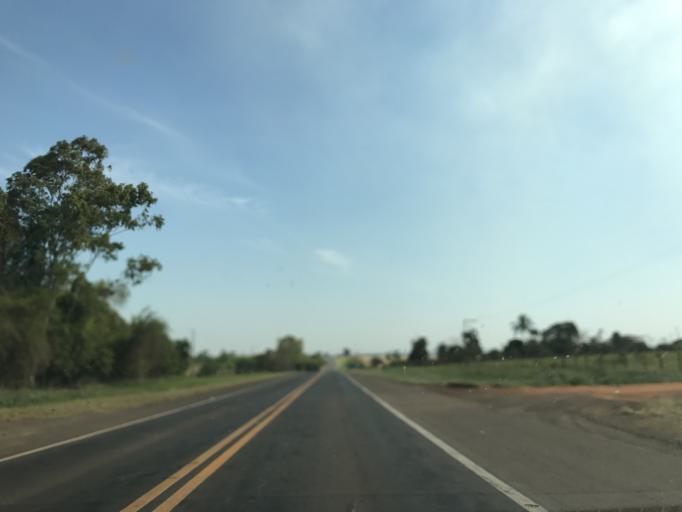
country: BR
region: Sao Paulo
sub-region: Penapolis
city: Penapolis
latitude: -21.4019
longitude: -50.1121
